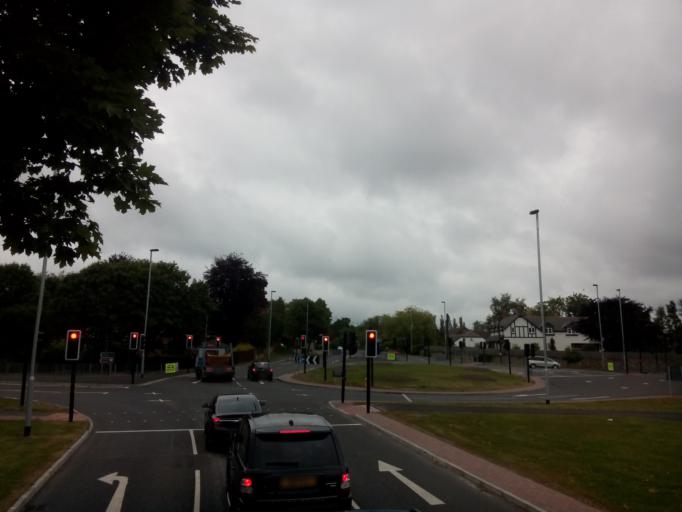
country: GB
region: England
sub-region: County Durham
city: Chester-le-Street
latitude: 54.8672
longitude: -1.5749
